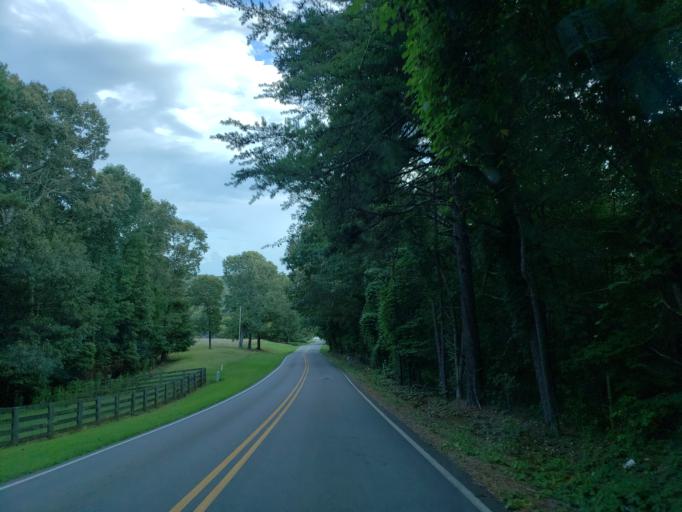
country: US
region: Georgia
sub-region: Cherokee County
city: Ball Ground
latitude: 34.3248
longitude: -84.4261
